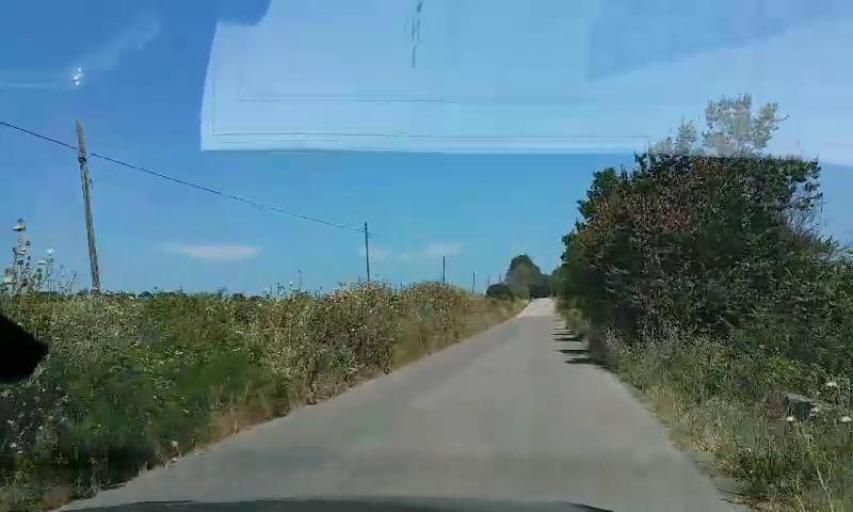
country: IT
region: Molise
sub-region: Provincia di Campobasso
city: Guglionesi
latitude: 41.9574
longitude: 14.9003
